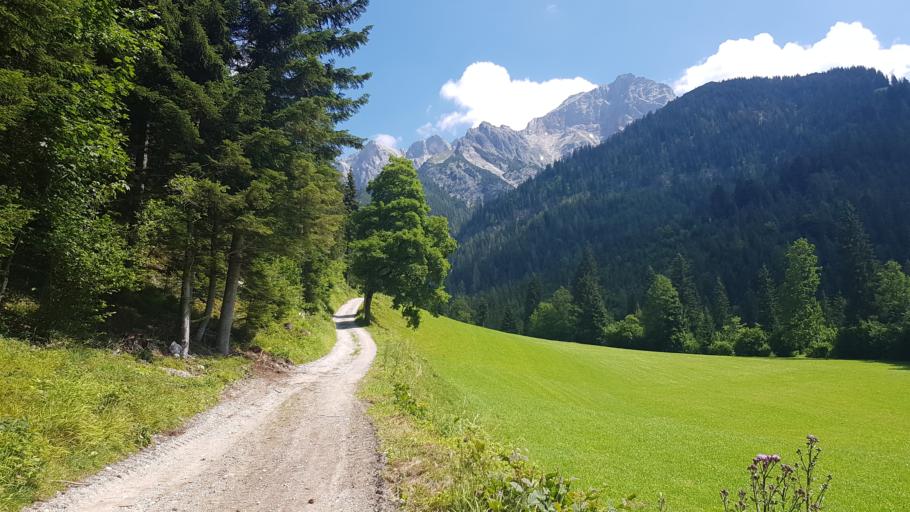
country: AT
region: Salzburg
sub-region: Politischer Bezirk Zell am See
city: Maria Alm am Steinernen Meer
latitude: 47.4223
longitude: 12.9320
